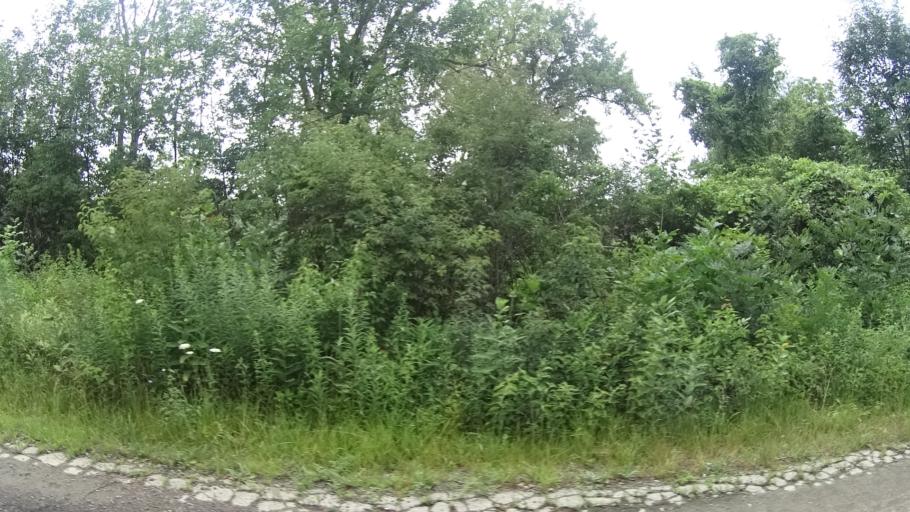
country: US
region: Ohio
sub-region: Erie County
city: Sandusky
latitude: 41.4436
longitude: -82.7407
